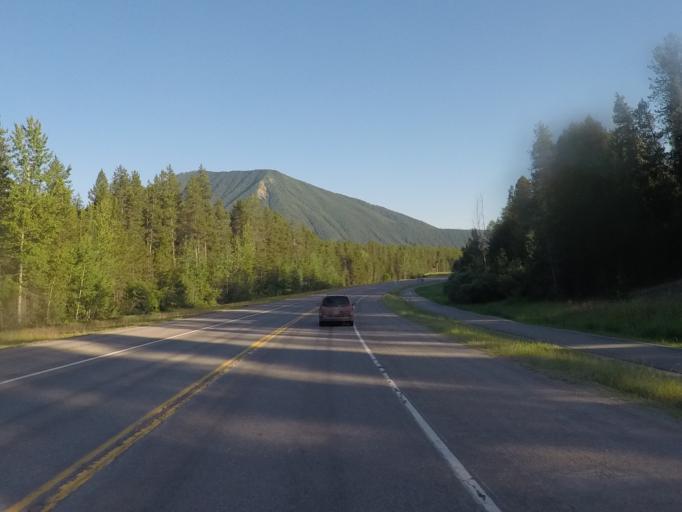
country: US
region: Montana
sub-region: Flathead County
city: Columbia Falls
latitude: 48.4710
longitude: -113.9971
